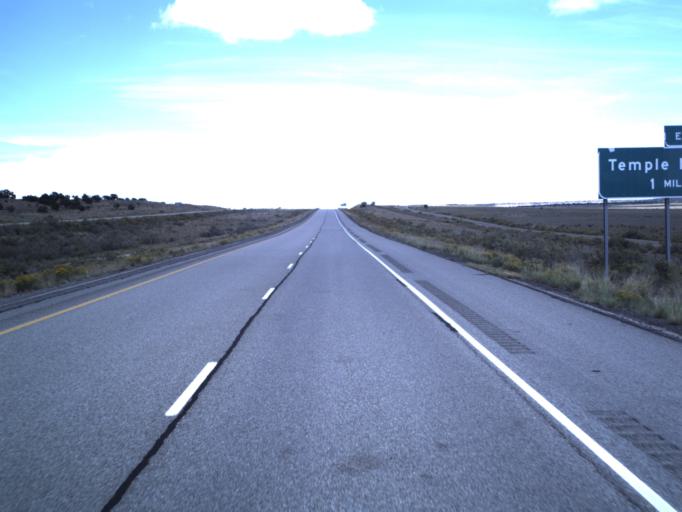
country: US
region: Utah
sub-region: Emery County
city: Castle Dale
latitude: 38.8733
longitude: -110.6792
